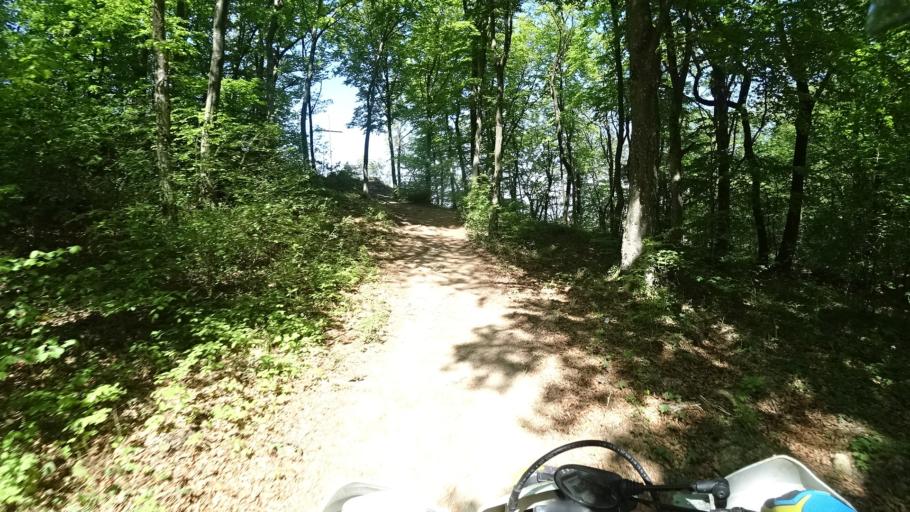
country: HR
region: Zagrebacka
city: Jablanovec
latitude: 45.8692
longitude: 15.8547
